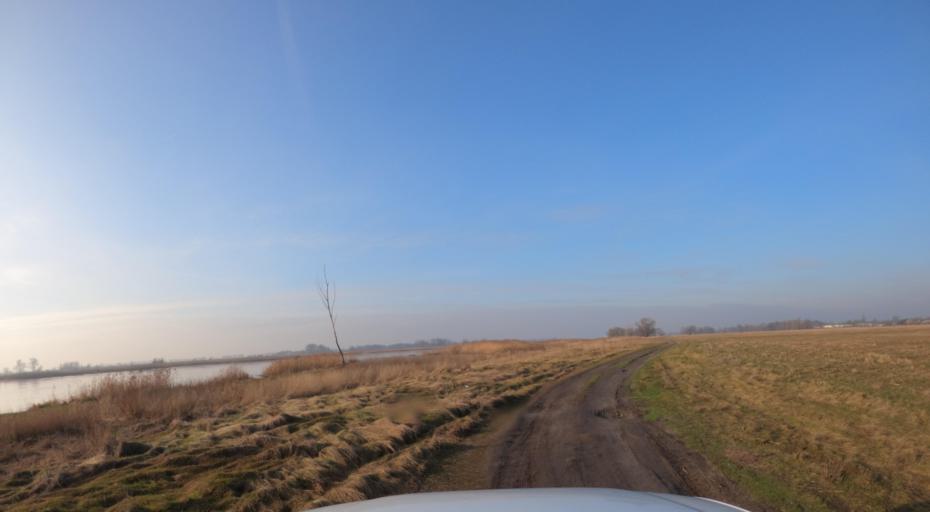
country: PL
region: Lubusz
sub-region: Powiat gorzowski
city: Kostrzyn nad Odra
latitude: 52.6139
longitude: 14.5914
